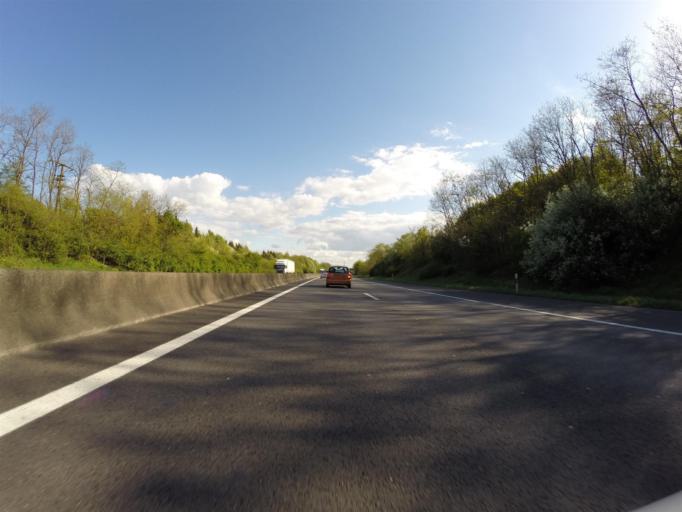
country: LU
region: Luxembourg
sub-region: Canton de Luxembourg
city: Hesperange
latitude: 49.5607
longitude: 6.1298
